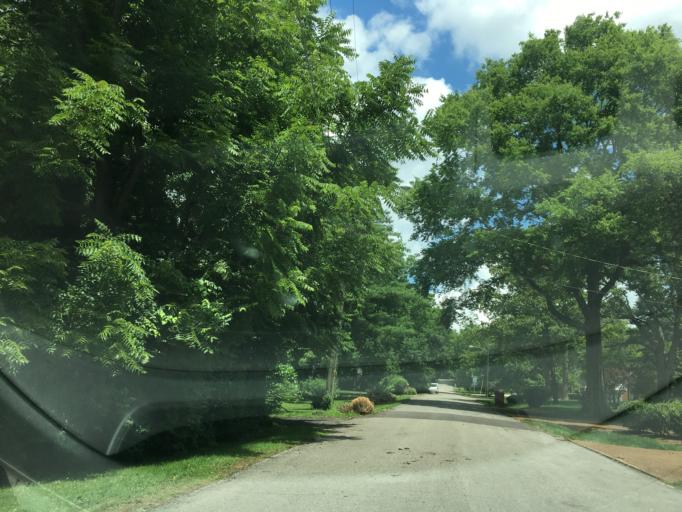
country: US
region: Tennessee
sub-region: Davidson County
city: Oak Hill
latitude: 36.0964
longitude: -86.7903
